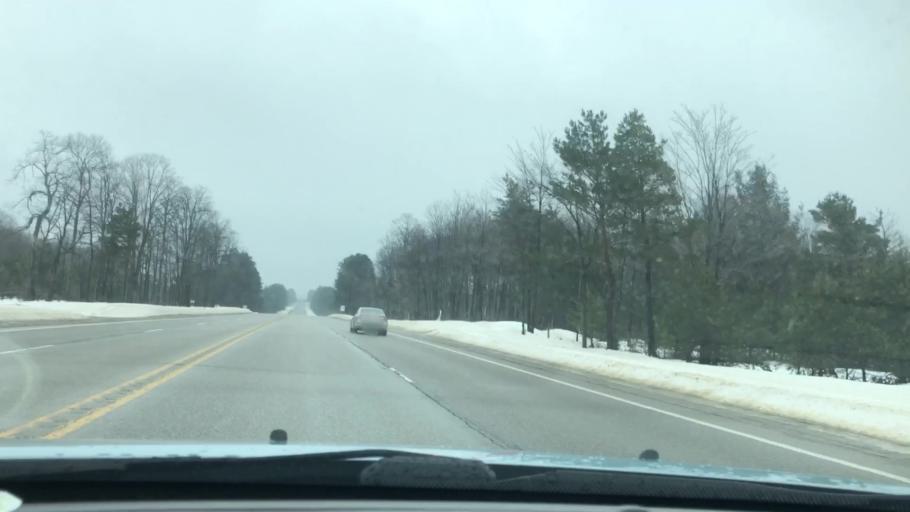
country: US
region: Michigan
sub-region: Otsego County
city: Gaylord
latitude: 45.0621
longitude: -84.8296
